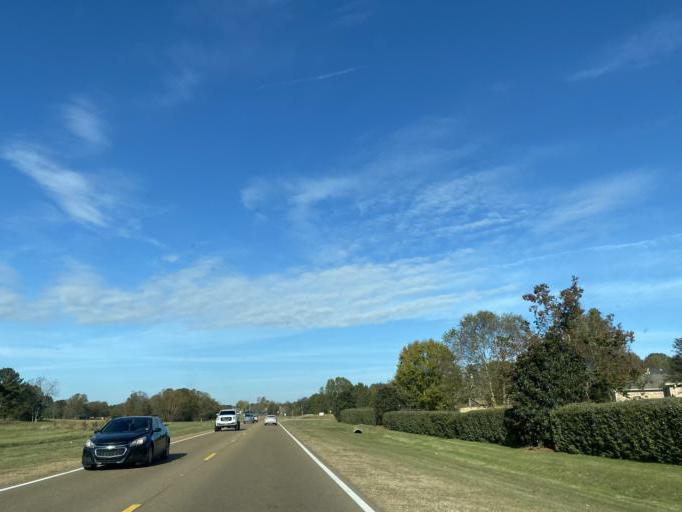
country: US
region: Mississippi
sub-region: Madison County
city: Madison
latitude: 32.4776
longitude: -90.1552
